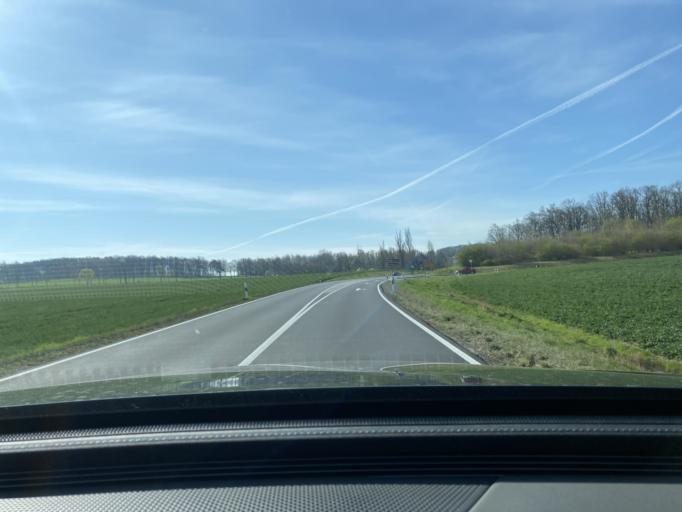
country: DE
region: Saxony
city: Radibor
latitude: 51.2081
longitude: 14.3736
